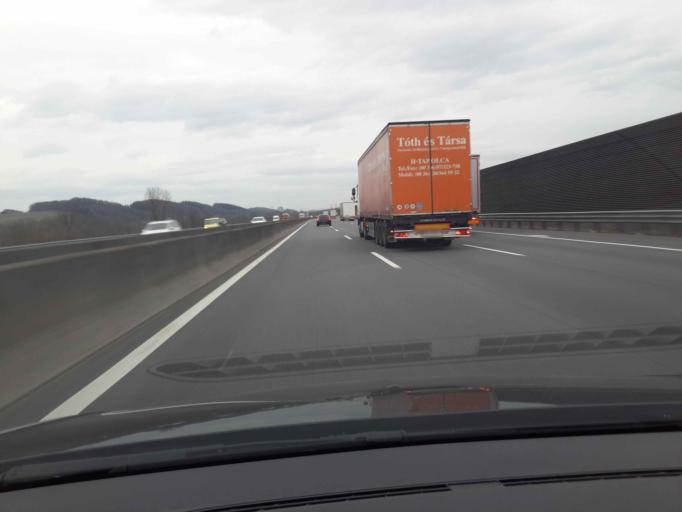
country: AT
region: Lower Austria
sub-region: Politischer Bezirk Melk
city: Neumarkt an der Ybbs
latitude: 48.1390
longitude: 15.0646
